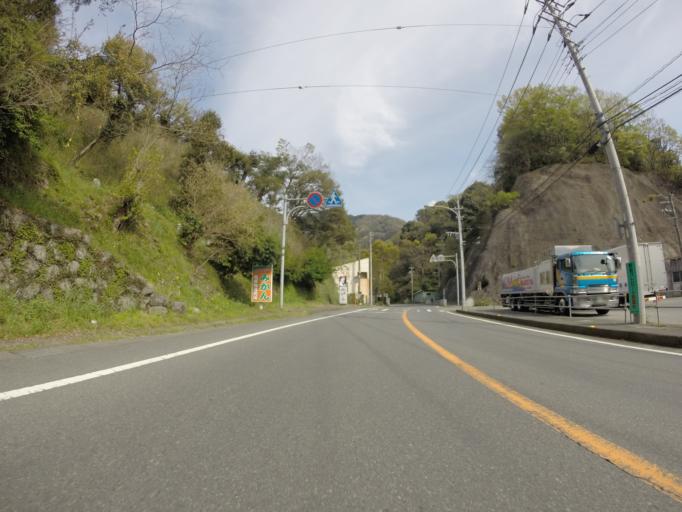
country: JP
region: Shizuoka
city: Numazu
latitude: 35.0175
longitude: 138.8886
